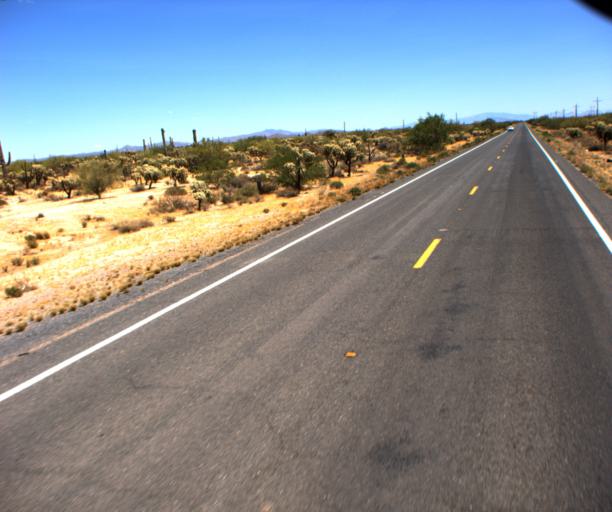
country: US
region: Arizona
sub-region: Pinal County
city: Florence
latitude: 32.9374
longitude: -111.3135
